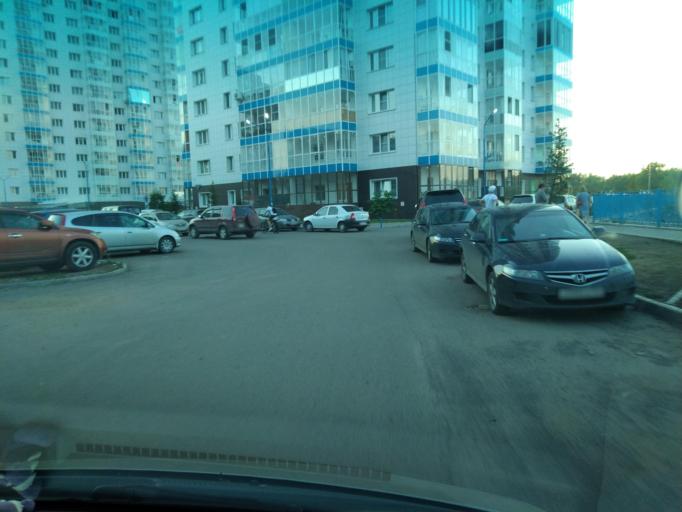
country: RU
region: Krasnoyarskiy
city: Krasnoyarsk
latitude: 55.9876
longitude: 92.8696
